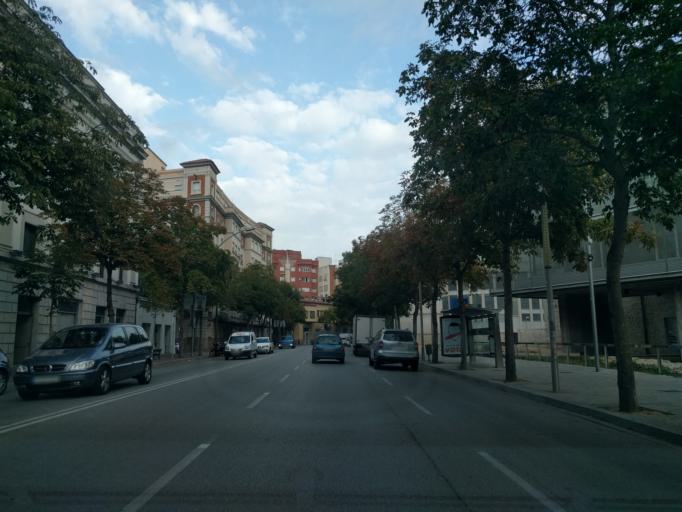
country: ES
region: Catalonia
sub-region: Provincia de Girona
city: Girona
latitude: 41.9803
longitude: 2.8214
